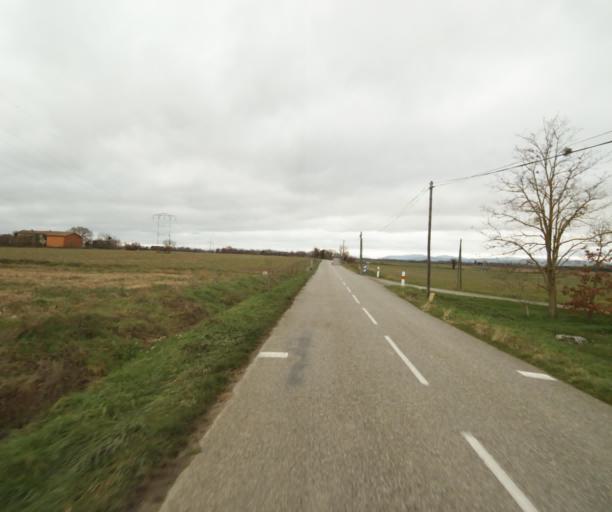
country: FR
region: Midi-Pyrenees
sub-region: Departement de l'Ariege
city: Mazeres
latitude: 43.1910
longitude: 1.6335
